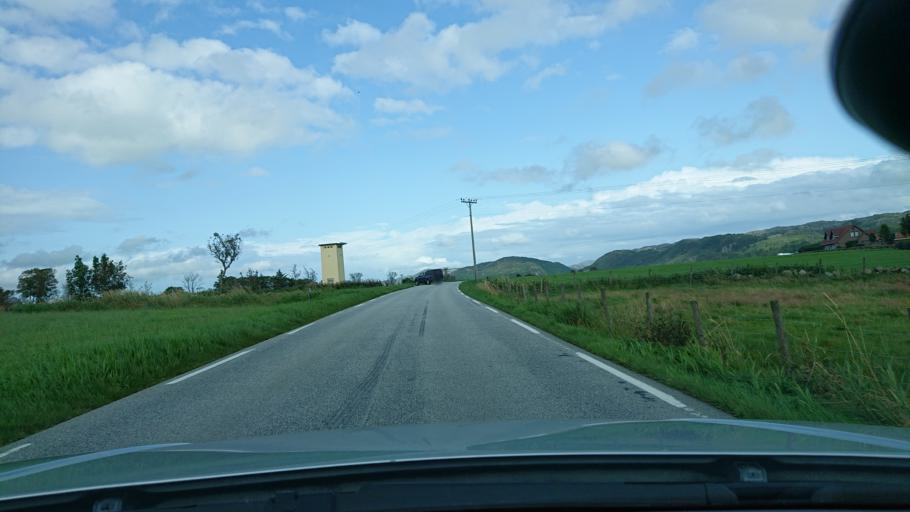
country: NO
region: Rogaland
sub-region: Gjesdal
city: Algard
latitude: 58.6921
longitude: 5.7714
